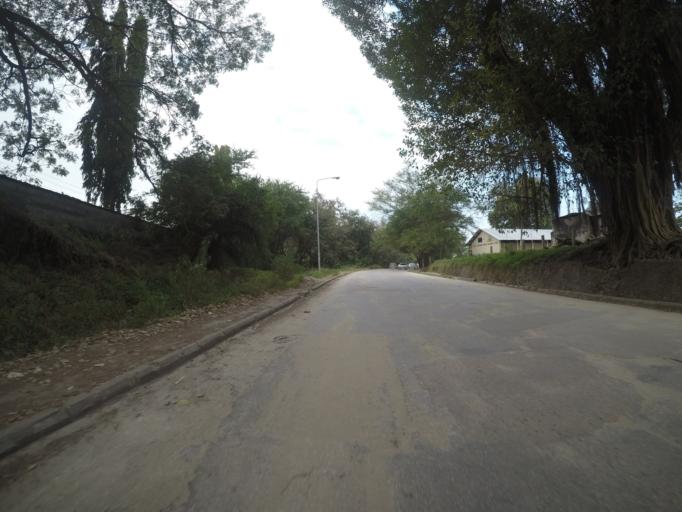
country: TZ
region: Zanzibar Urban/West
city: Zanzibar
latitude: -6.1747
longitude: 39.2052
